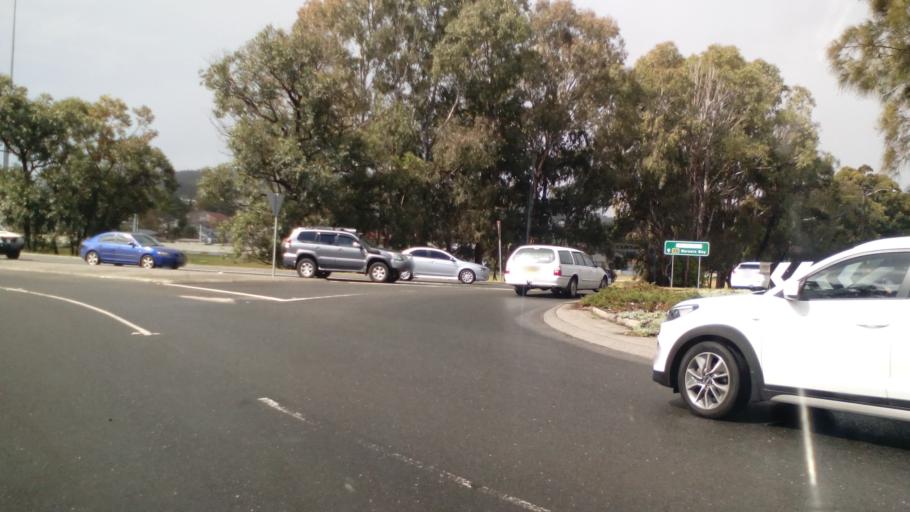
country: AU
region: New South Wales
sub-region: Lake Macquarie Shire
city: Glendale
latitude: -32.9572
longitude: 151.6170
